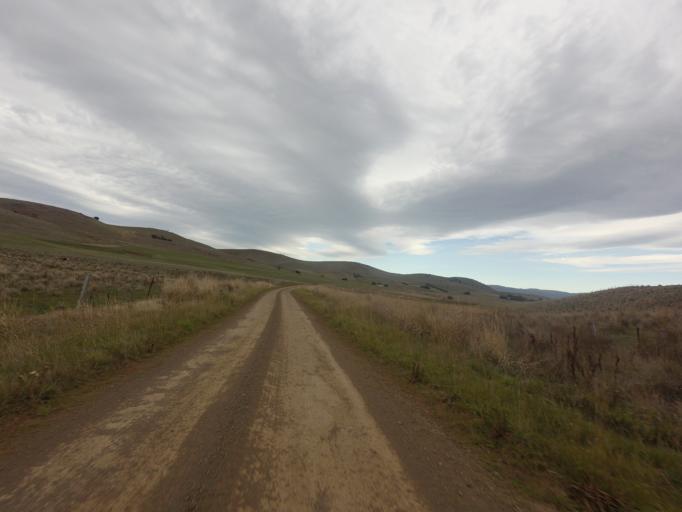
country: AU
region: Tasmania
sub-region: Derwent Valley
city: New Norfolk
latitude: -42.4397
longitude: 146.8031
